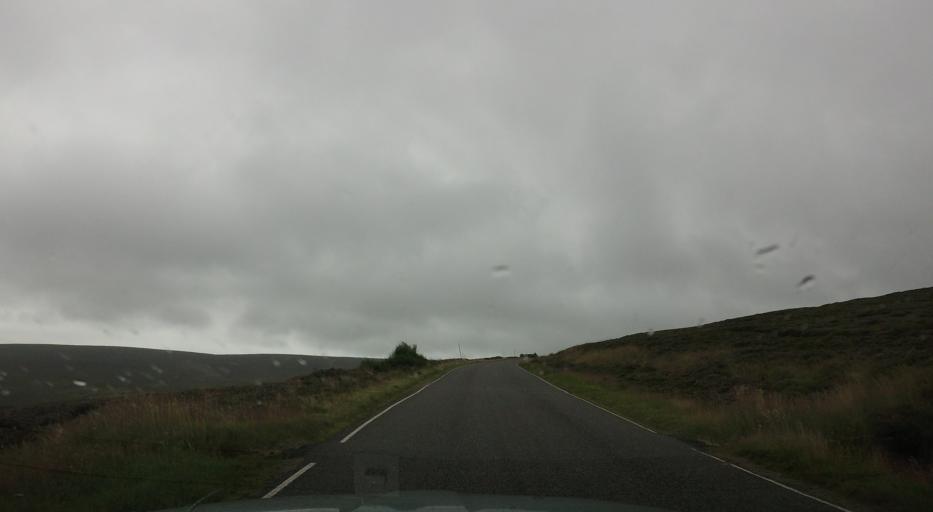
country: GB
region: Scotland
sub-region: Aberdeenshire
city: Laurencekirk
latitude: 56.9324
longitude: -2.5711
